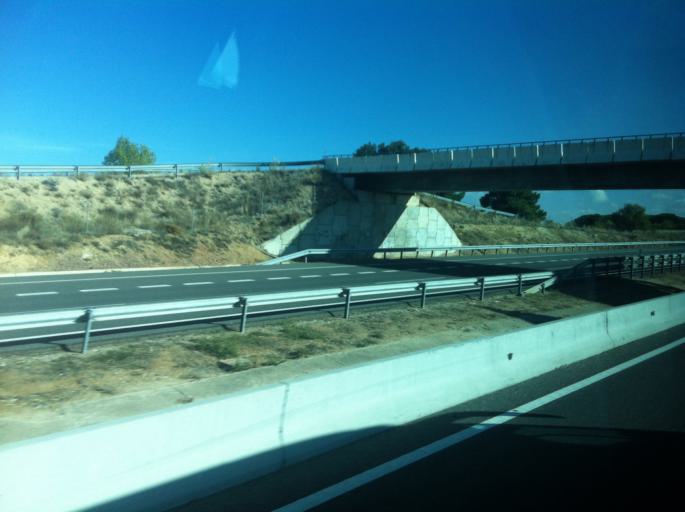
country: ES
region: Castille and Leon
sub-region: Provincia de Burgos
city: Fuentespina
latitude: 41.6270
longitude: -3.6930
